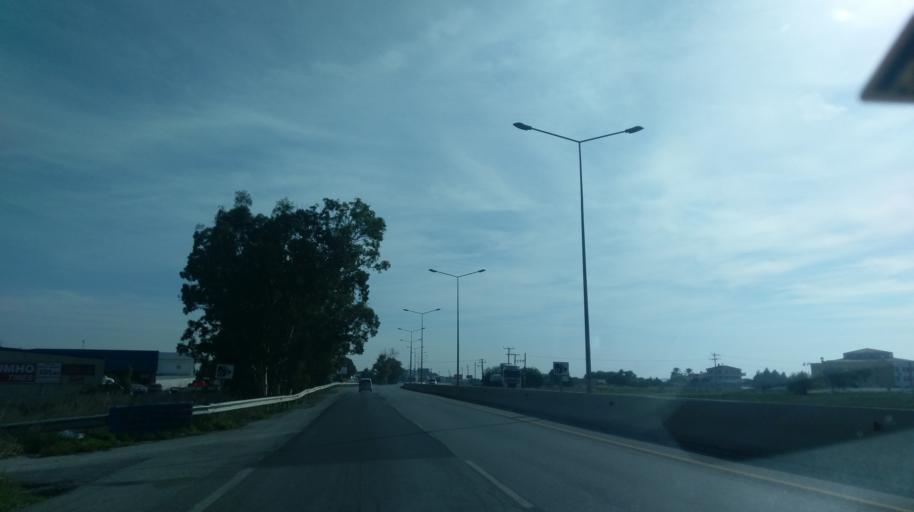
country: CY
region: Lefkosia
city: Geri
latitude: 35.2161
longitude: 33.5094
